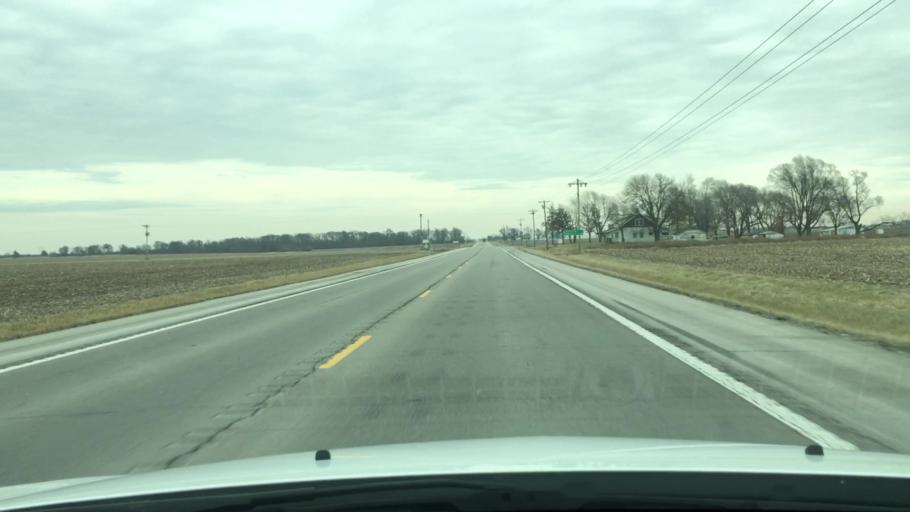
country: US
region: Missouri
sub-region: Audrain County
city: Mexico
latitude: 39.1638
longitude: -91.7645
